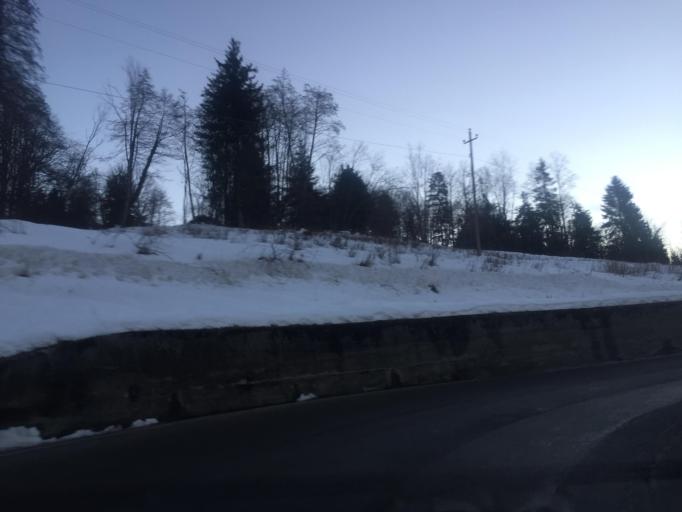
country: IT
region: Friuli Venezia Giulia
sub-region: Provincia di Udine
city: Lauco
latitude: 46.4267
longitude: 12.9249
